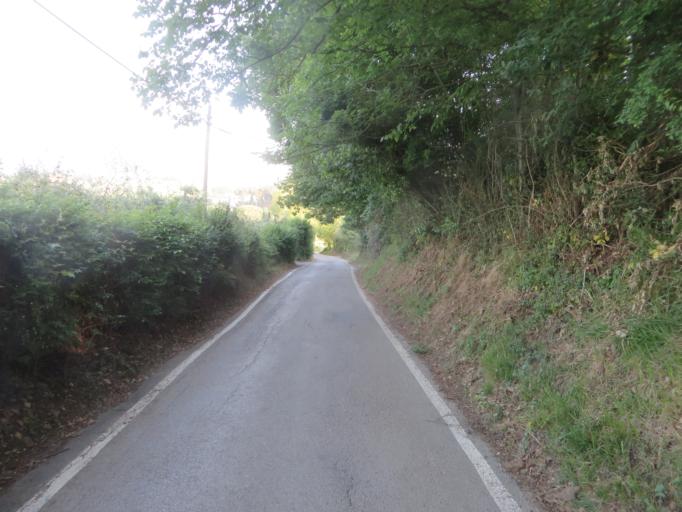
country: IT
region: Tuscany
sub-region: Province of Florence
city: Bagno a Ripoli
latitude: 43.7483
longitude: 11.3205
